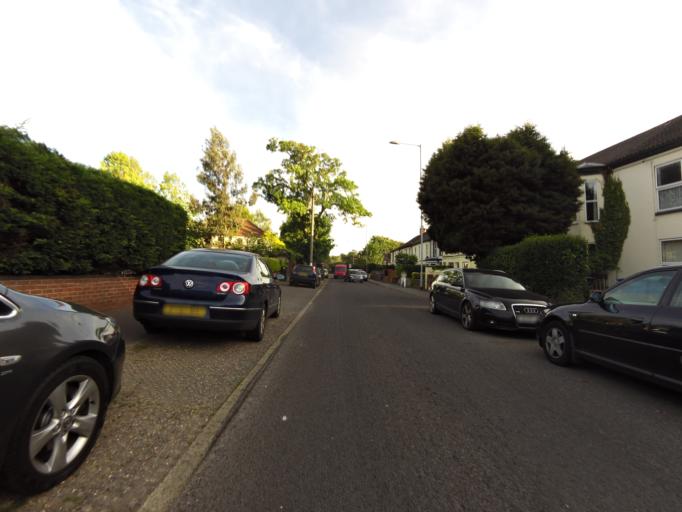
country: GB
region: England
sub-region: Norfolk
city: Norwich
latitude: 52.6489
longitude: 1.2912
